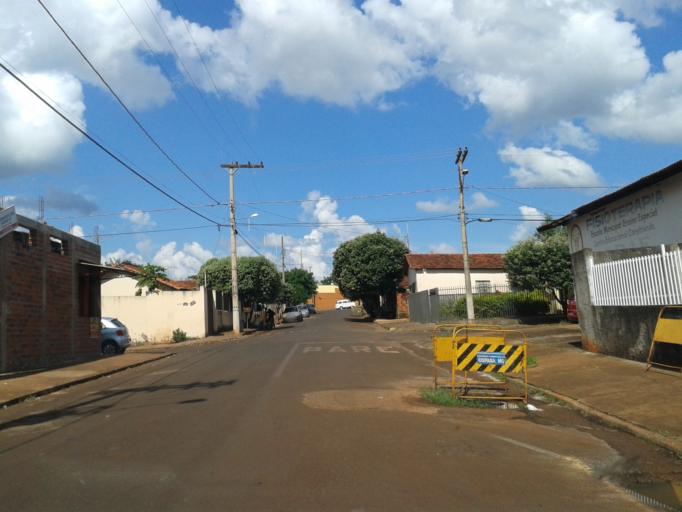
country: BR
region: Minas Gerais
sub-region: Capinopolis
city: Capinopolis
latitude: -18.6848
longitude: -49.5768
